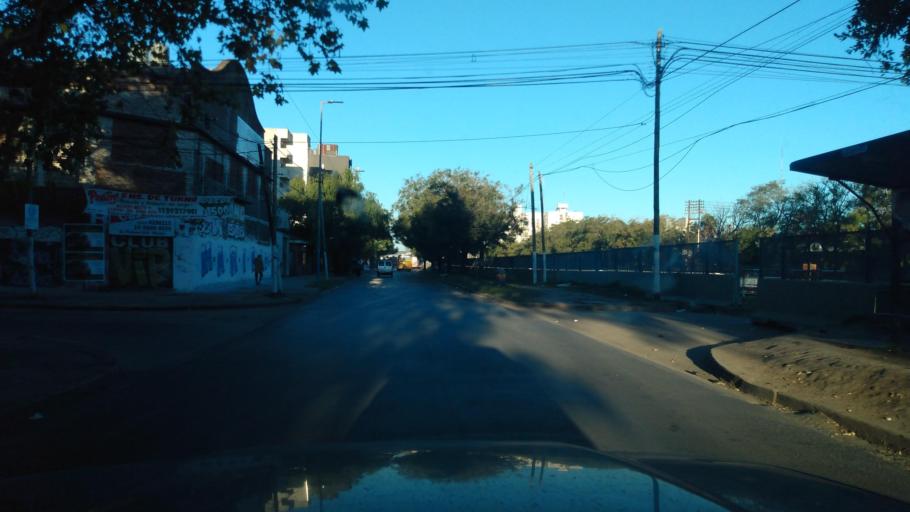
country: AR
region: Buenos Aires
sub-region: Partido de Merlo
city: Merlo
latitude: -34.6486
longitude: -58.7959
